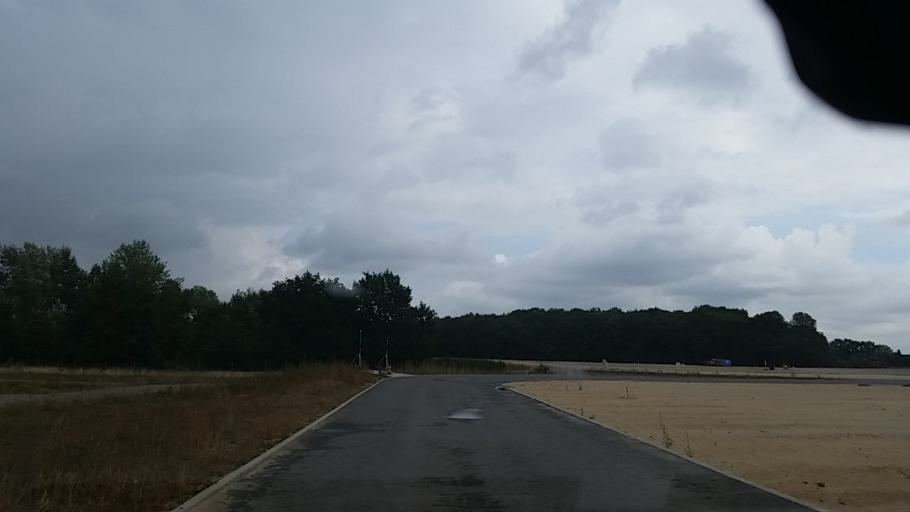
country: DE
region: Lower Saxony
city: Wolfsburg
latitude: 52.4250
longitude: 10.8312
